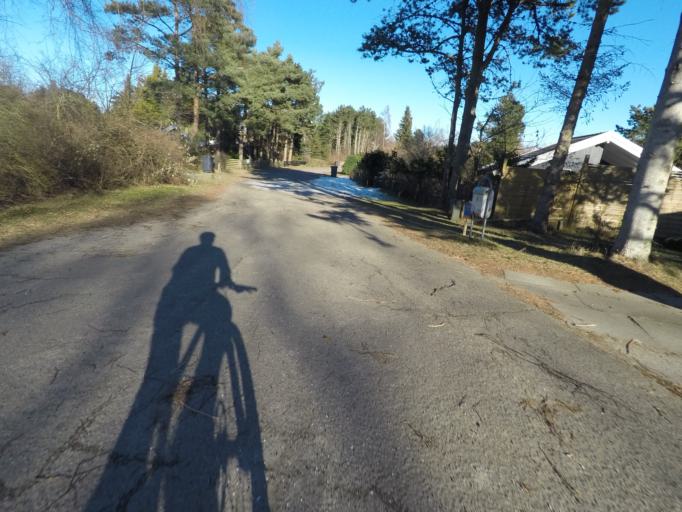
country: DK
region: Capital Region
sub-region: Halsnaes Kommune
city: Liseleje
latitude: 55.9993
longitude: 11.9336
